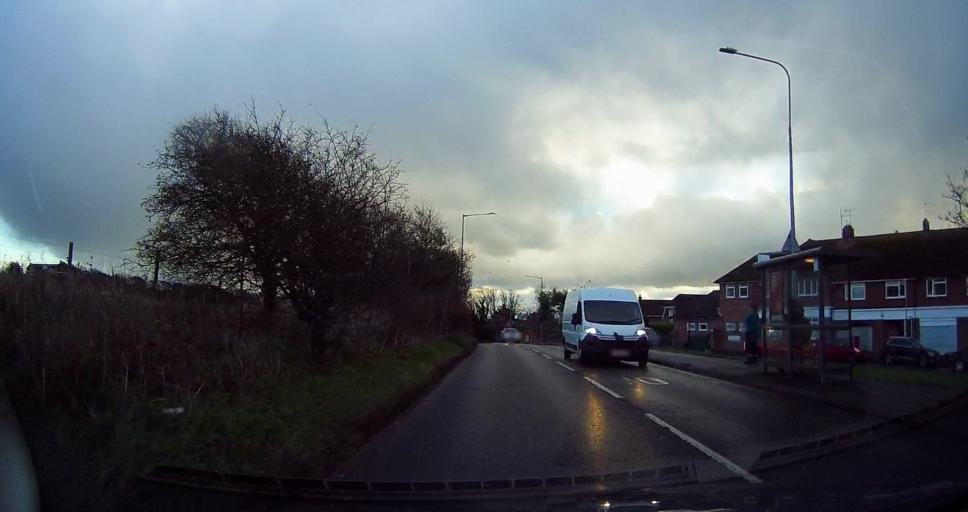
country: GB
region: England
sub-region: Brighton and Hove
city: Rottingdean
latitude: 50.8124
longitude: -0.0619
